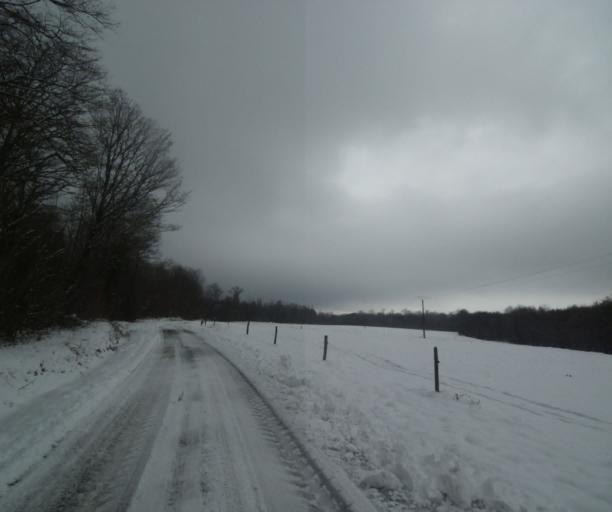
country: FR
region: Champagne-Ardenne
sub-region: Departement de la Haute-Marne
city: Laneuville-a-Remy
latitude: 48.4666
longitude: 4.8989
